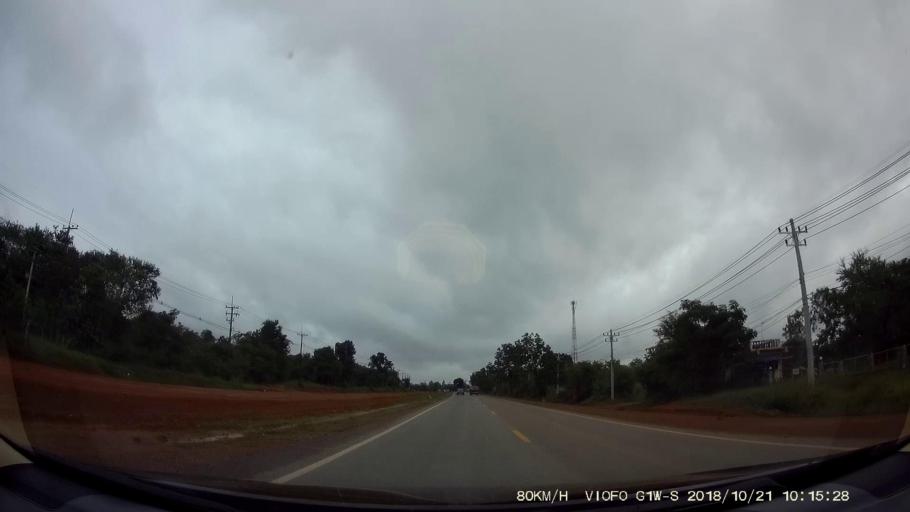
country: TH
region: Chaiyaphum
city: Phu Khiao
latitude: 16.3409
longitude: 102.1656
